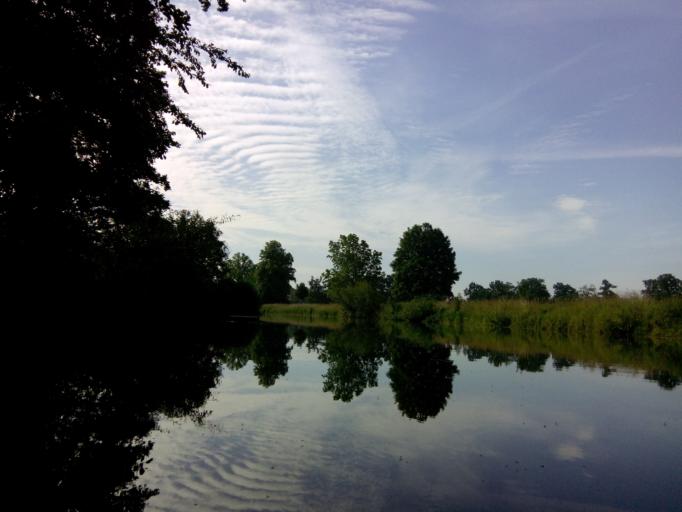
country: NL
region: Utrecht
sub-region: Gemeente Utrecht
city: Lunetten
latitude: 52.0693
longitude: 5.1563
